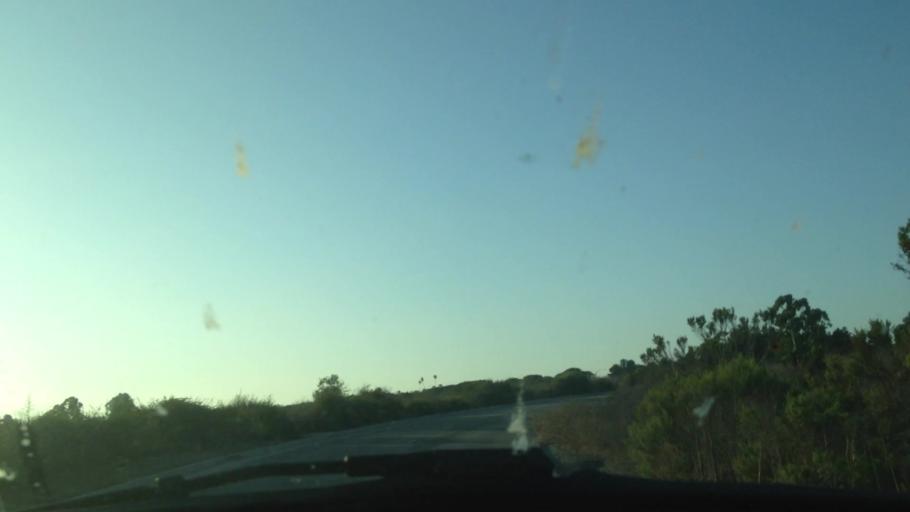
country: US
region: California
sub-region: Orange County
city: San Joaquin Hills
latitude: 33.5837
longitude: -117.8521
